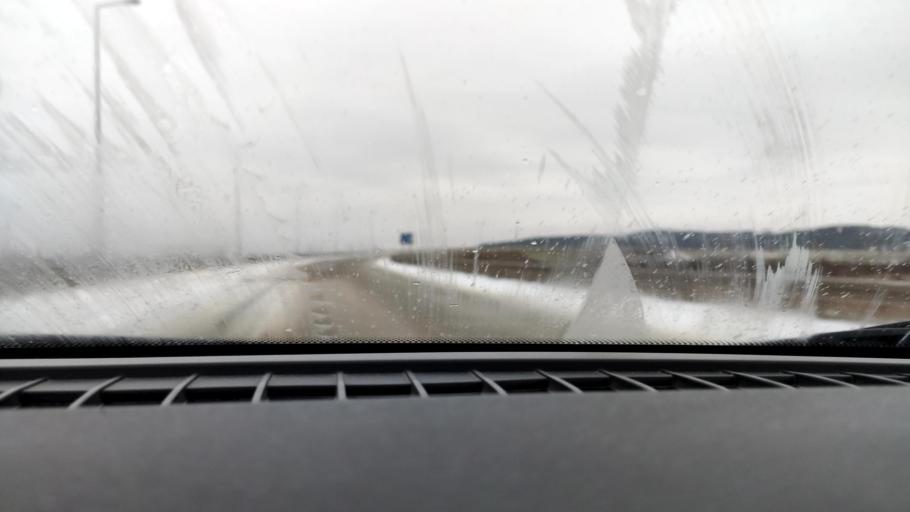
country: RU
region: Perm
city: Kondratovo
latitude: 57.9254
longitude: 56.1743
